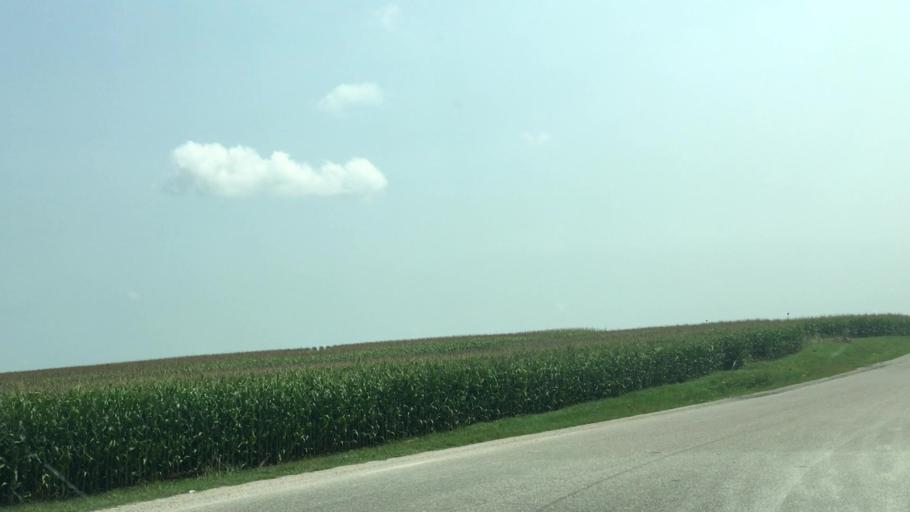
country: US
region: Iowa
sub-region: Benton County
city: Urbana
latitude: 42.2478
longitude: -91.8905
